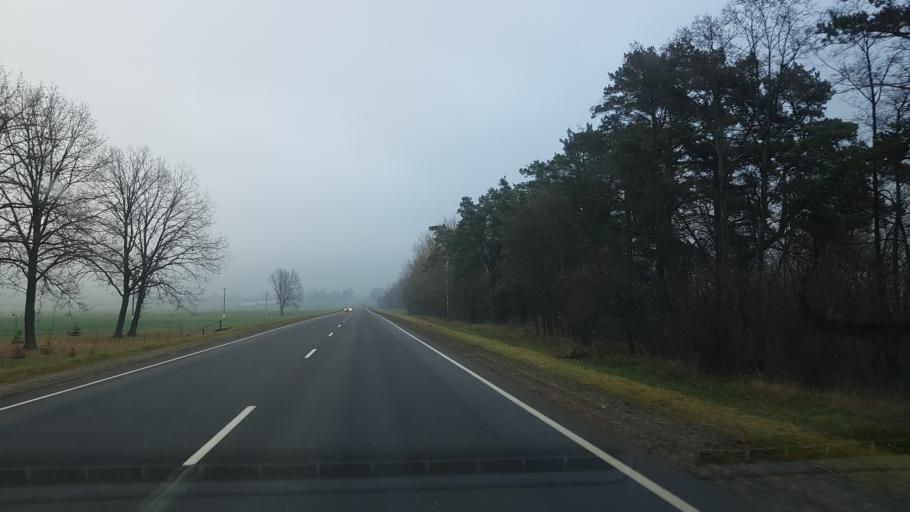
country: BY
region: Mogilev
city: Babruysk
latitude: 53.1685
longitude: 29.3335
